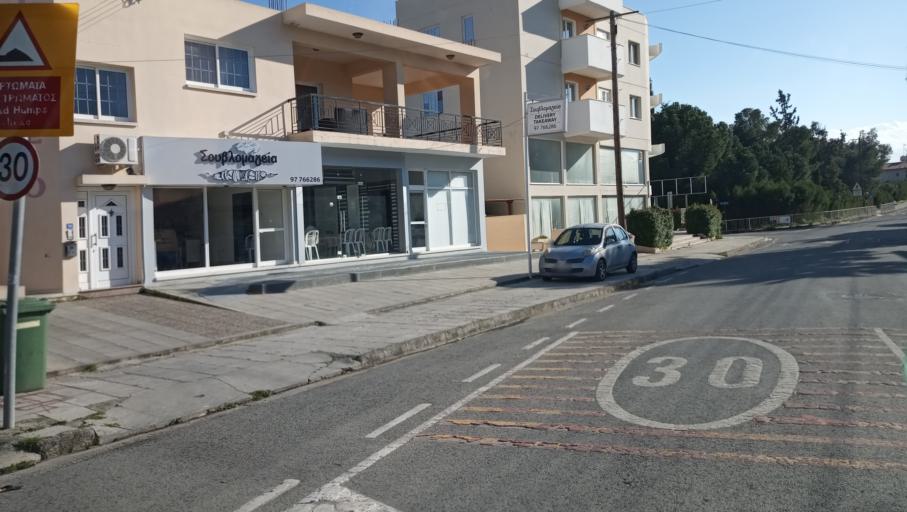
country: CY
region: Lefkosia
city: Nicosia
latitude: 35.1421
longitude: 33.3186
